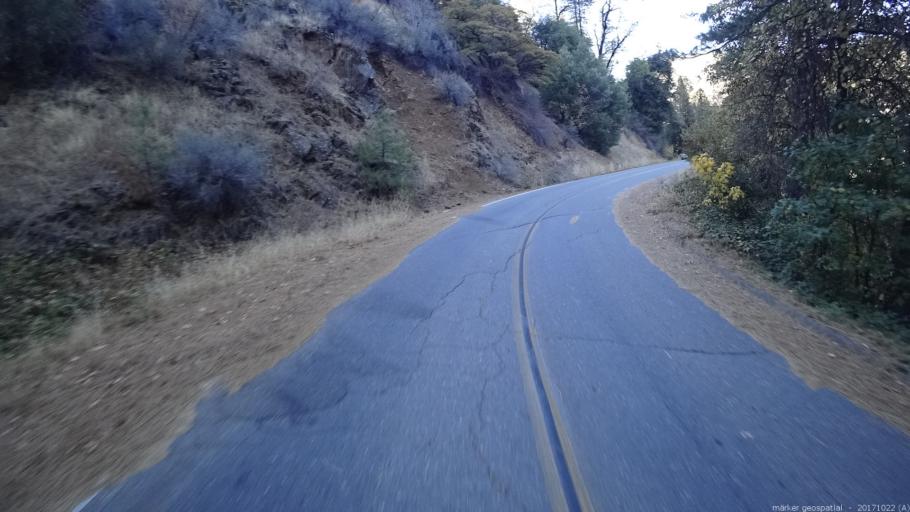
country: US
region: California
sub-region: Shasta County
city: Shasta Lake
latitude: 40.9160
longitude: -122.2467
